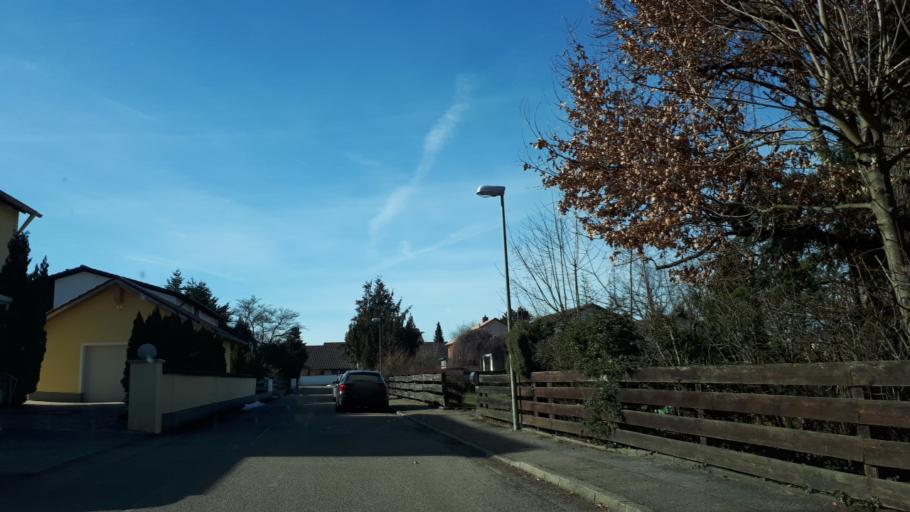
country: DE
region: Bavaria
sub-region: Upper Palatinate
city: Pentling
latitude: 48.9810
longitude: 12.0563
